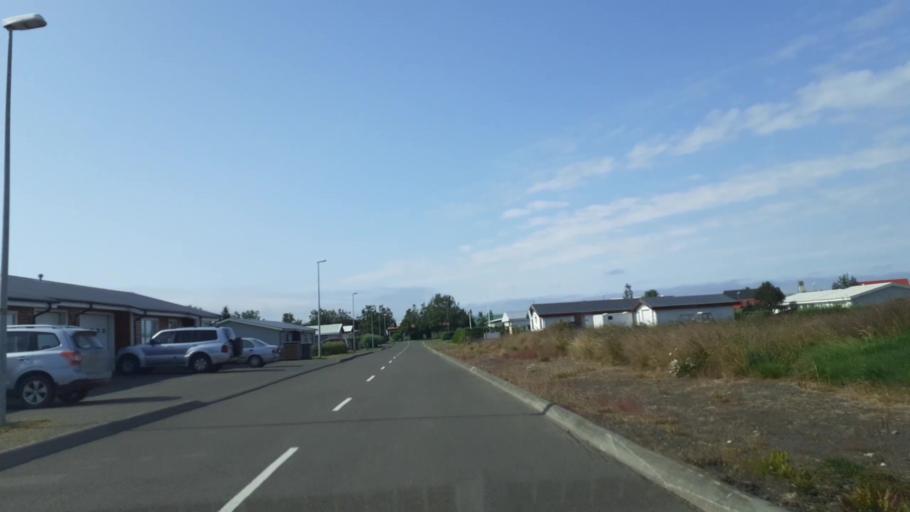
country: IS
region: Northwest
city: Saudarkrokur
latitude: 65.6642
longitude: -20.2865
